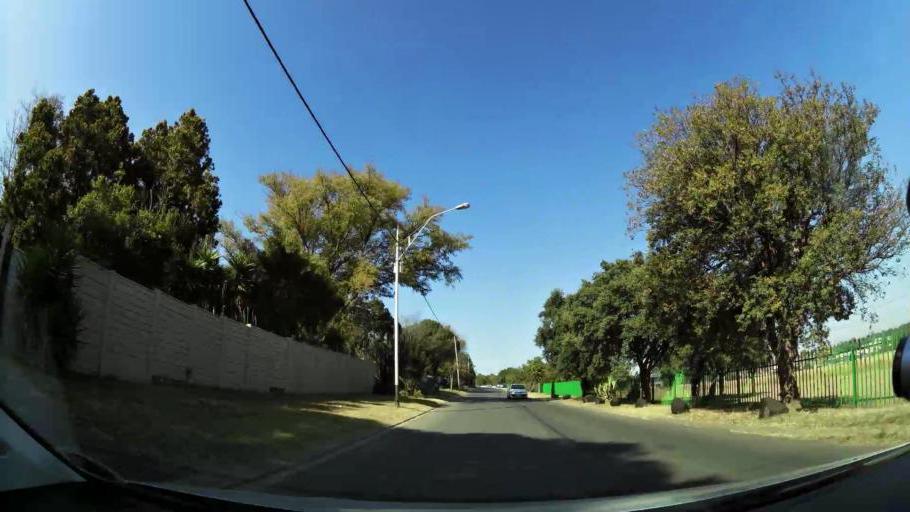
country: ZA
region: Gauteng
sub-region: City of Johannesburg Metropolitan Municipality
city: Modderfontein
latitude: -26.1174
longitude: 28.1153
